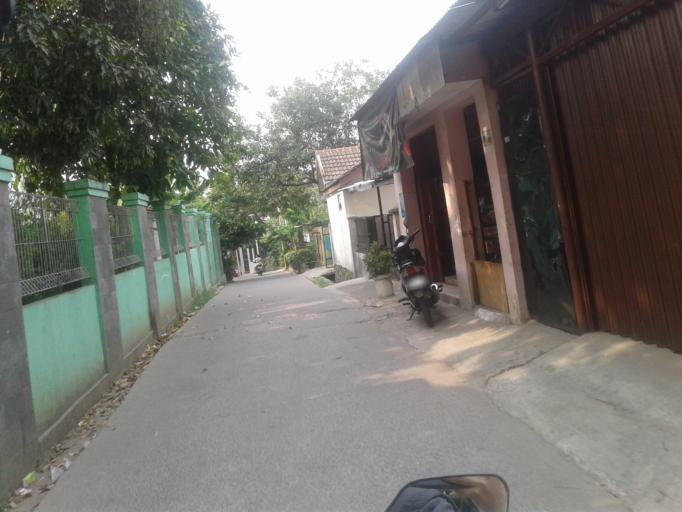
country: ID
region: West Java
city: Depok
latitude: -6.3759
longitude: 106.8370
